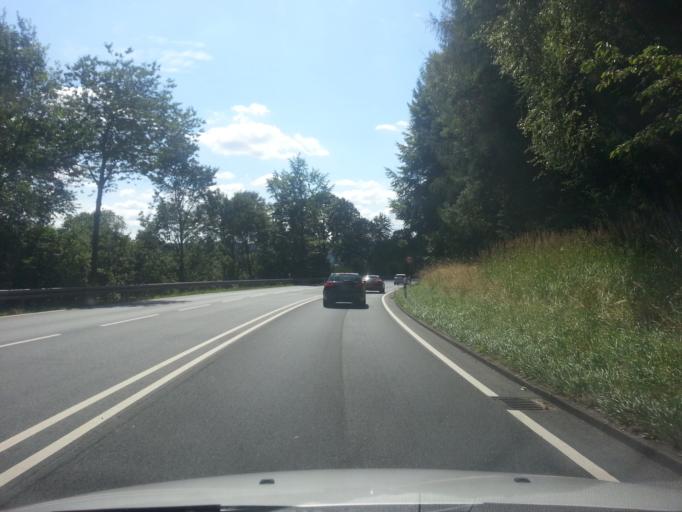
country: DE
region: Hesse
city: Hochst im Odenwald
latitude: 49.8114
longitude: 8.9729
